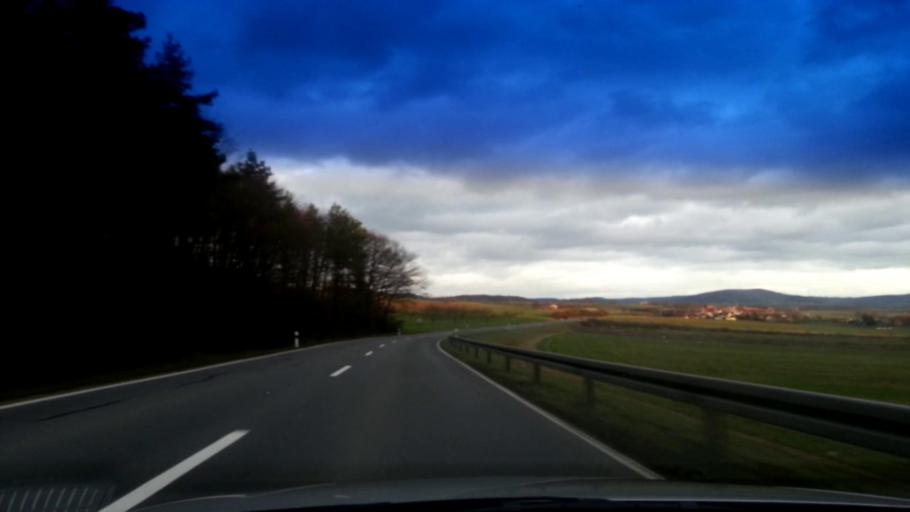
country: DE
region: Bavaria
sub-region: Upper Franconia
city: Zapfendorf
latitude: 49.9979
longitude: 10.9772
